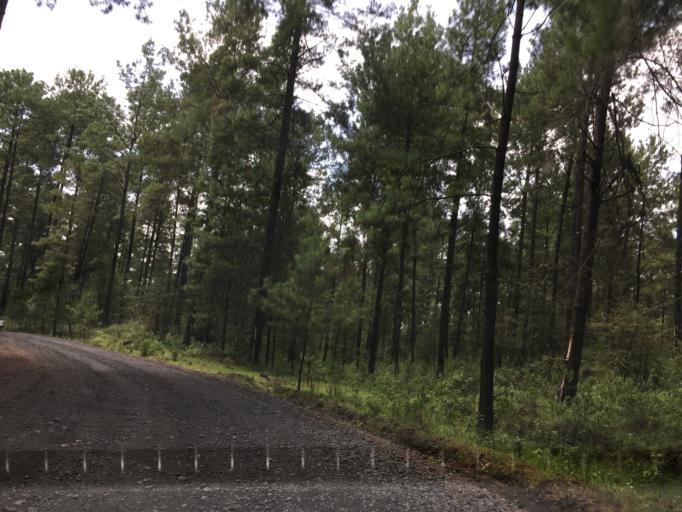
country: MX
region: Michoacan
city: Nuevo San Juan Parangaricutiro
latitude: 19.4541
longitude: -102.1866
